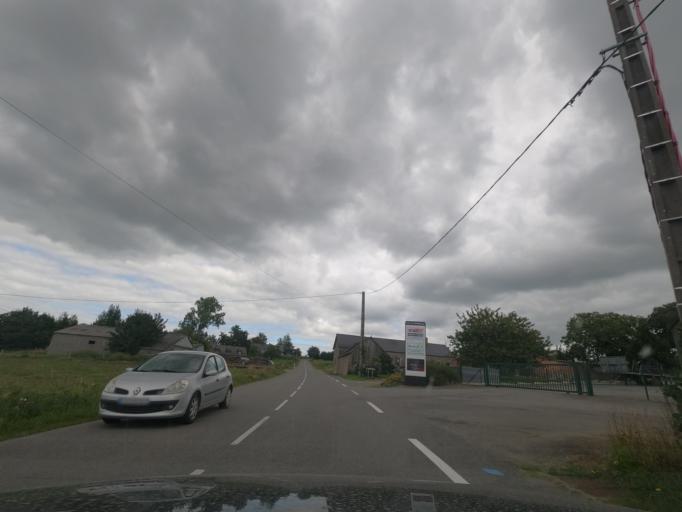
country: FR
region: Brittany
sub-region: Departement d'Ille-et-Vilaine
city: Landean
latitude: 48.4199
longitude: -1.1389
